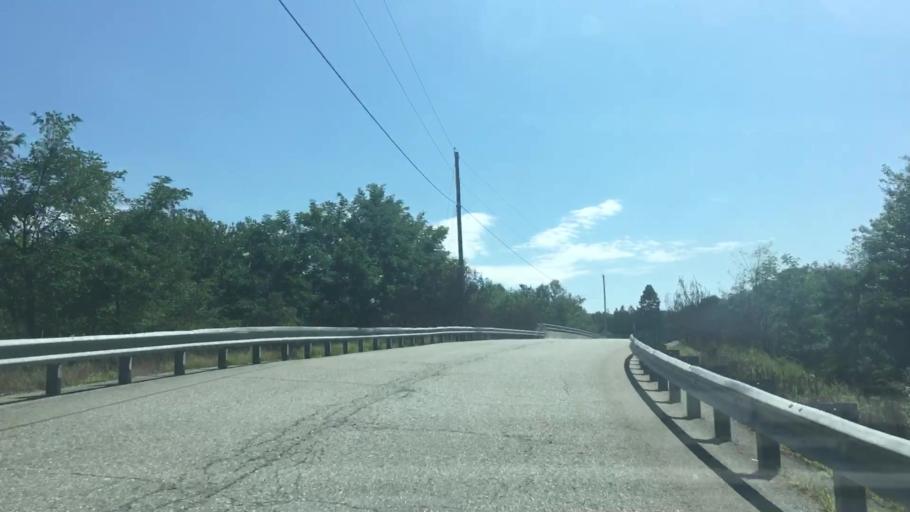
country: US
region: Maine
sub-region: Androscoggin County
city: Sabattus
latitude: 44.1249
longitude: -70.0361
